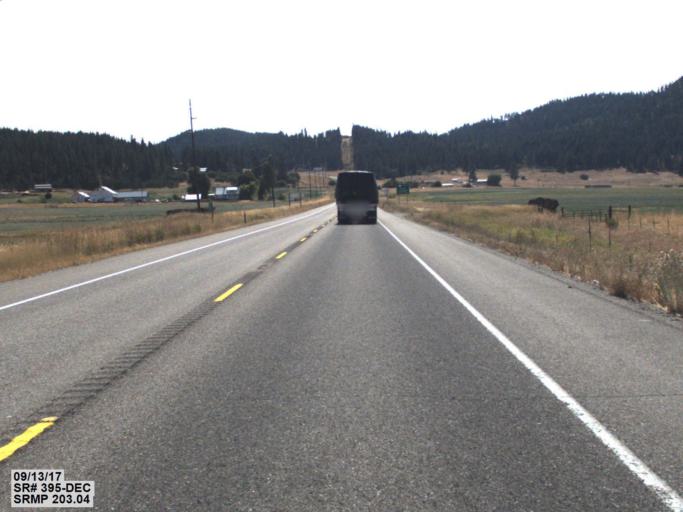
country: US
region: Washington
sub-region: Stevens County
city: Chewelah
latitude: 48.2170
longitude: -117.7154
